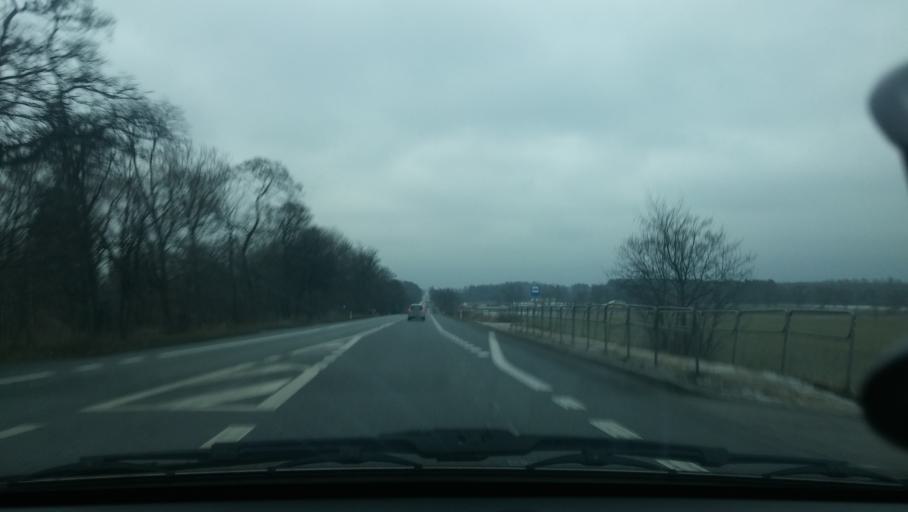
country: PL
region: Masovian Voivodeship
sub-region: Powiat wegrowski
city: Grebkow
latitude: 52.2024
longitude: 21.9686
